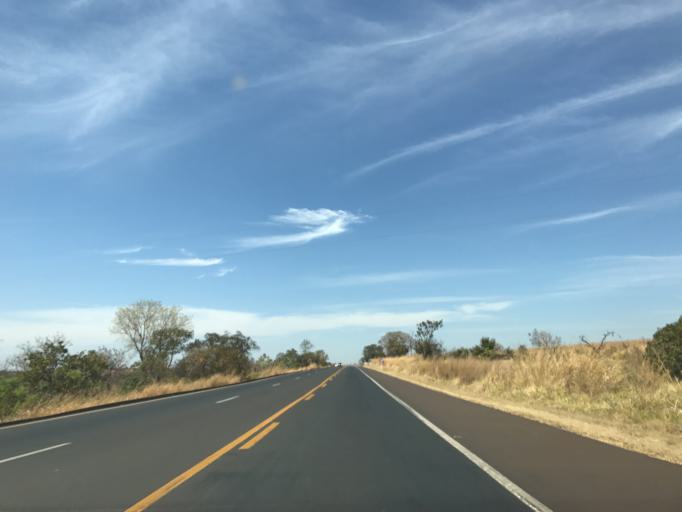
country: BR
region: Minas Gerais
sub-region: Monte Alegre De Minas
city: Monte Alegre de Minas
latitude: -18.9214
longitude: -49.0339
